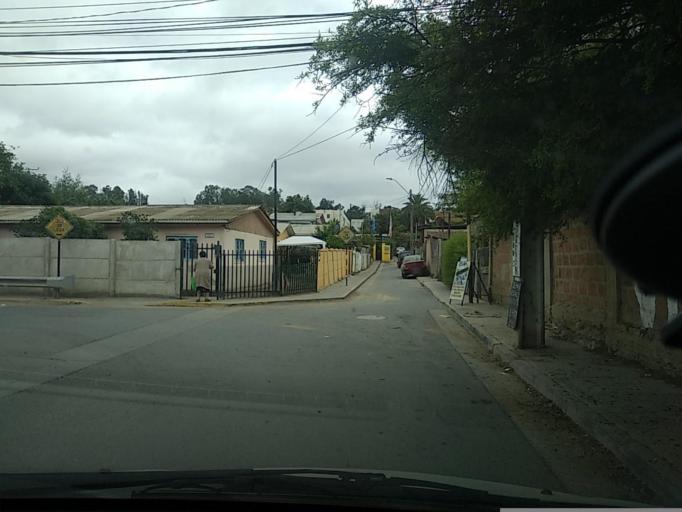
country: CL
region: Valparaiso
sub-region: Provincia de Marga Marga
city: Villa Alemana
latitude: -33.0373
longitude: -71.3588
